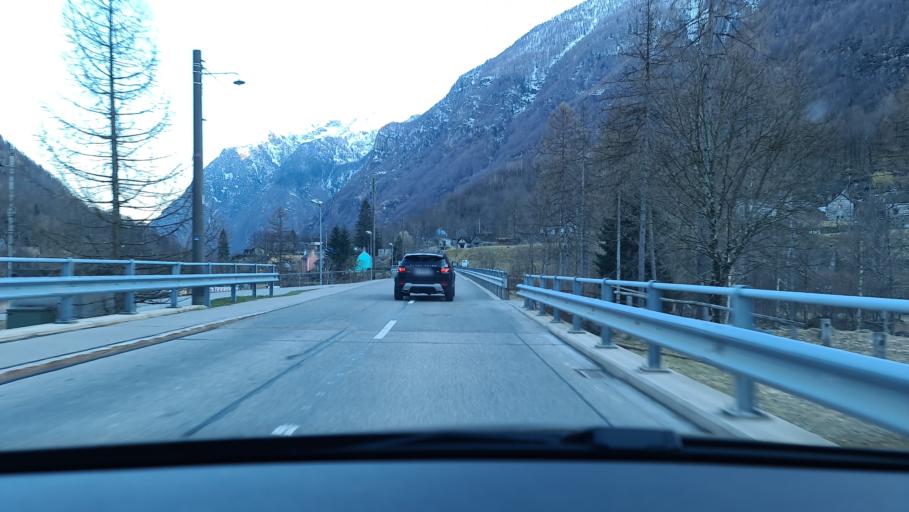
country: CH
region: Ticino
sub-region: Locarno District
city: Lavertezzo
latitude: 46.2939
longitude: 8.7927
